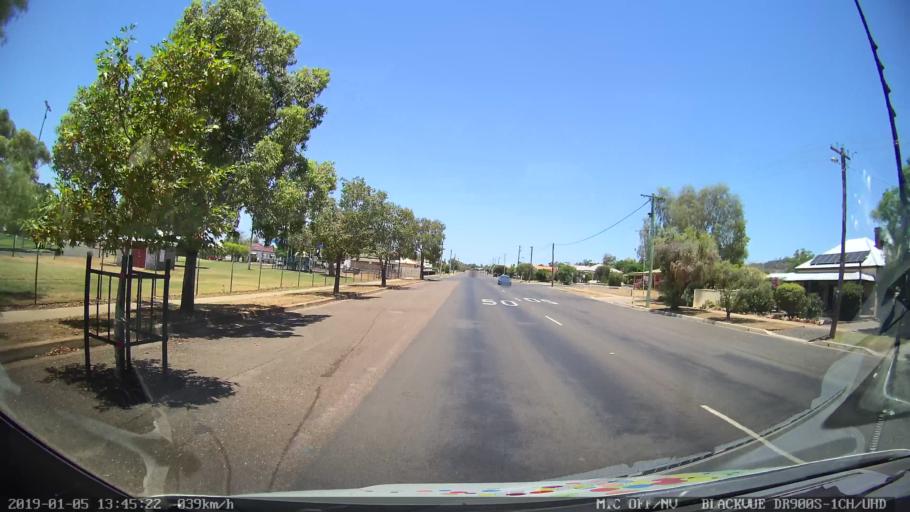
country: AU
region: New South Wales
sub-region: Gunnedah
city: Gunnedah
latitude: -30.9827
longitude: 150.2612
